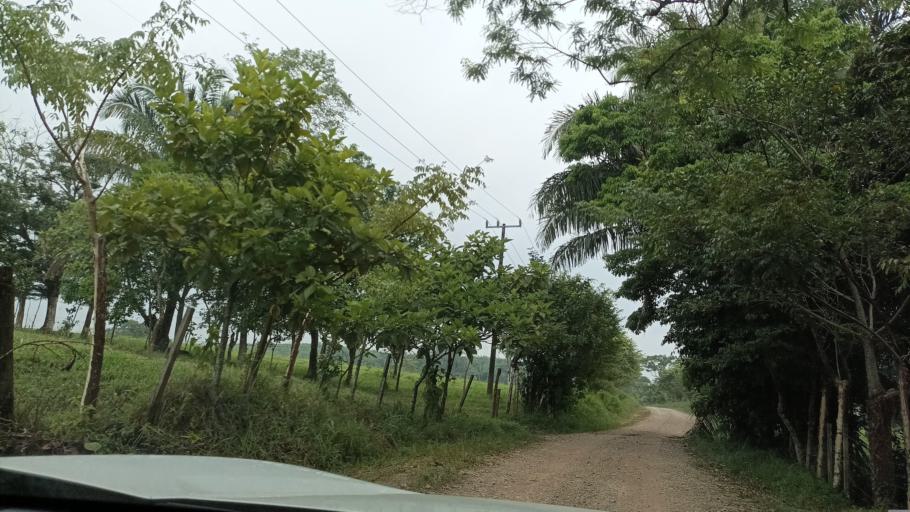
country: MX
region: Veracruz
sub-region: Uxpanapa
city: Poblado 10
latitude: 17.5464
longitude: -94.2335
